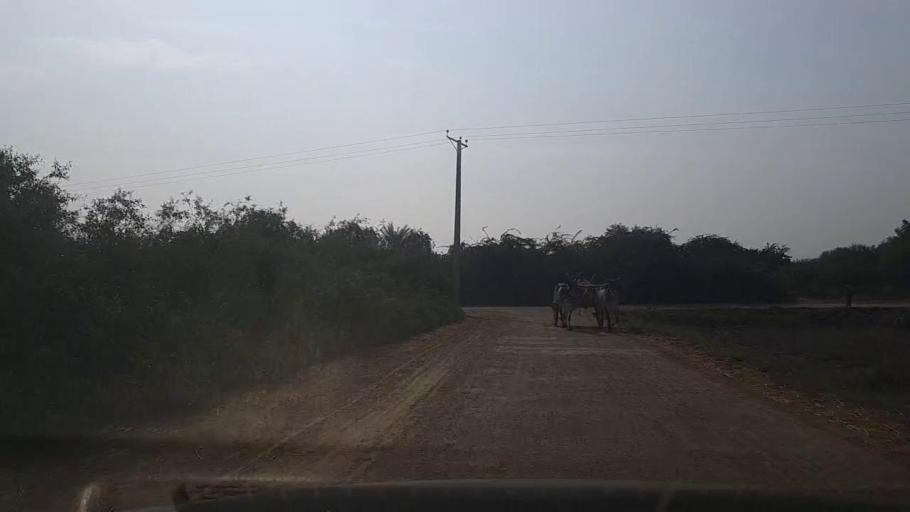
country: PK
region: Sindh
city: Bulri
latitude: 25.0079
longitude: 68.3000
